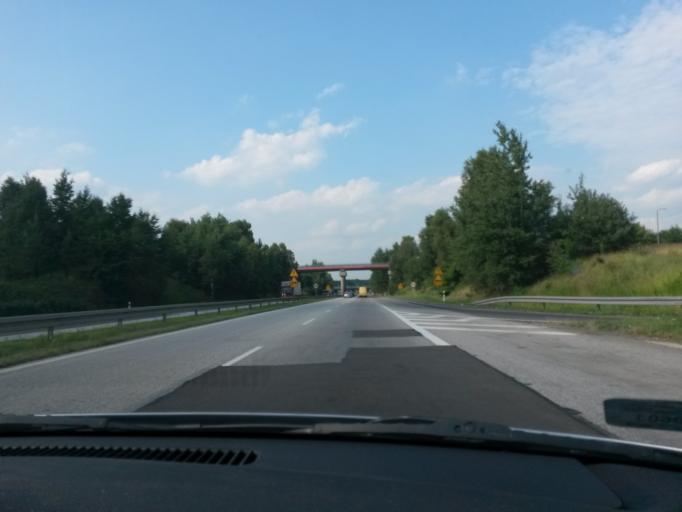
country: PL
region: Silesian Voivodeship
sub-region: Dabrowa Gornicza
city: Dabrowa Gornicza
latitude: 50.2861
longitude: 19.2170
